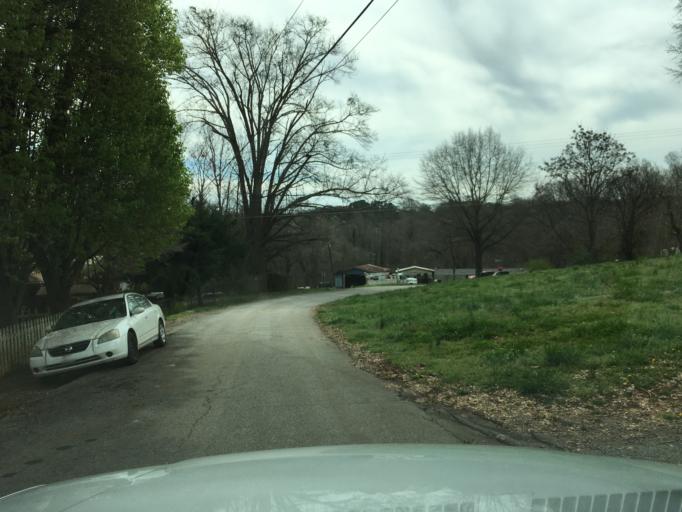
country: US
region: South Carolina
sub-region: Spartanburg County
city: Wellford
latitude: 34.8991
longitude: -82.0600
